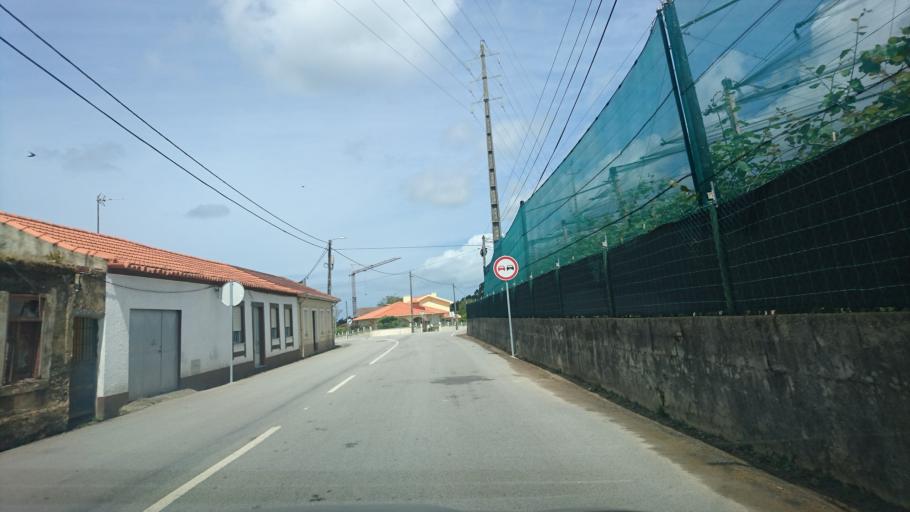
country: PT
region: Aveiro
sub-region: Santa Maria da Feira
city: Feira
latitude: 40.9172
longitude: -8.5805
